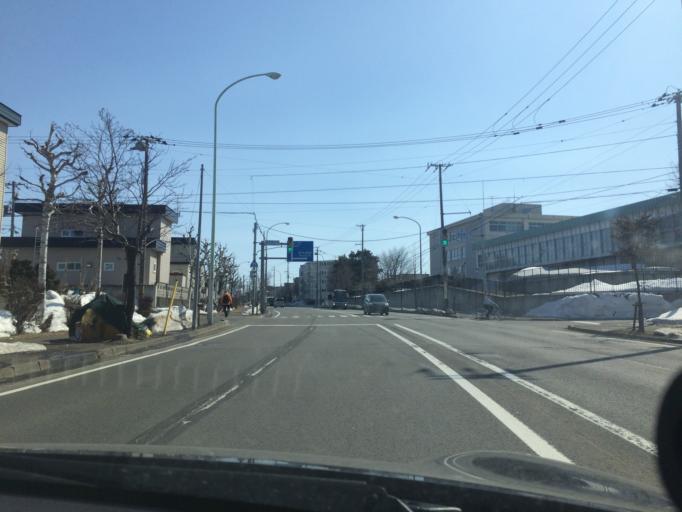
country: JP
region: Hokkaido
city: Ebetsu
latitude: 43.0484
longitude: 141.4876
